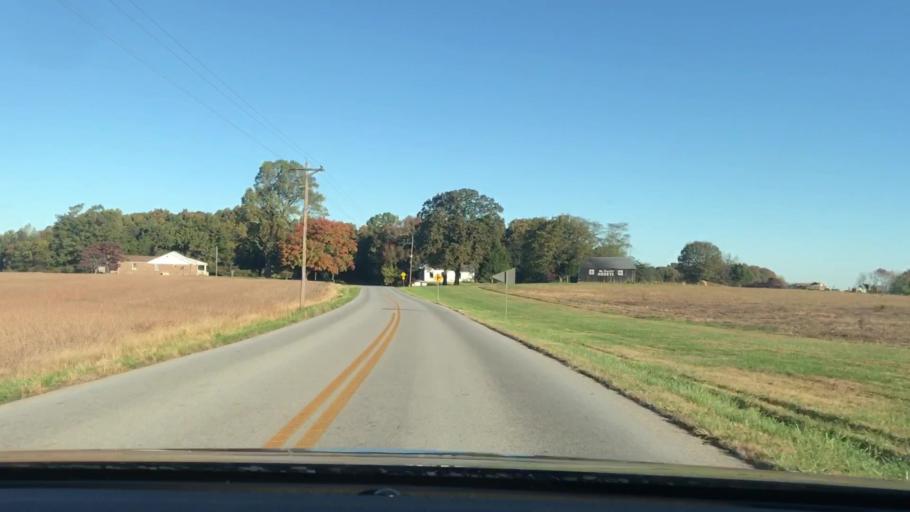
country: US
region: Kentucky
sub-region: Simpson County
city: Franklin
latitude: 36.7964
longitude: -86.6293
